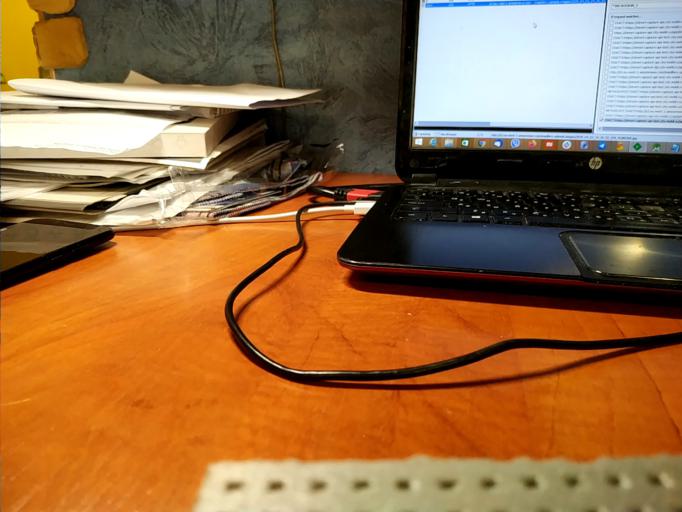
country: RU
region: Tverskaya
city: Spirovo
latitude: 57.4511
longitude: 34.9206
